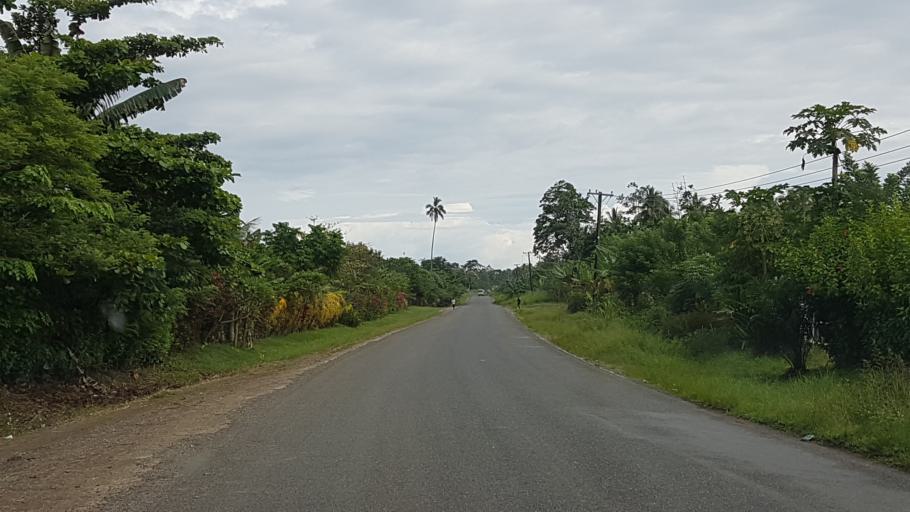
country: PG
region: Madang
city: Madang
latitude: -5.1572
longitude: 145.7794
